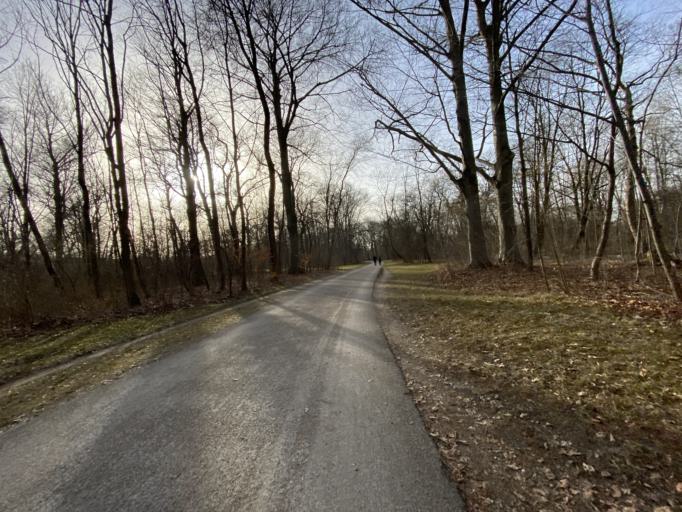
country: DE
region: Bavaria
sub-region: Upper Bavaria
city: Bogenhausen
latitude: 48.1801
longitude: 11.6165
